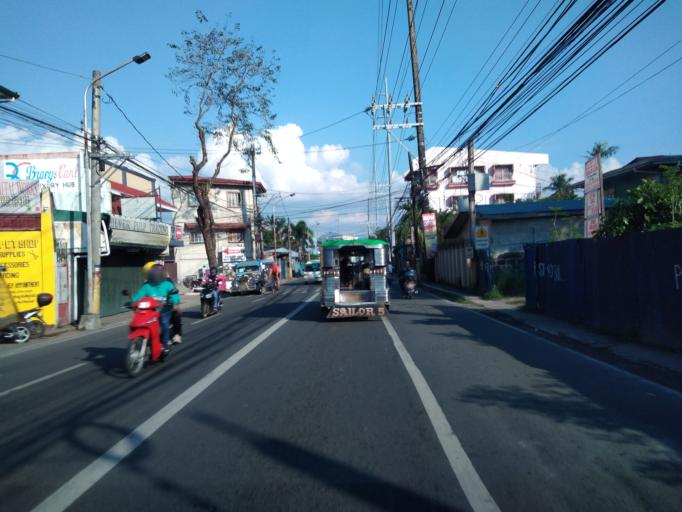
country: PH
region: Calabarzon
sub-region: Province of Laguna
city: Los Banos
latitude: 14.1797
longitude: 121.2360
